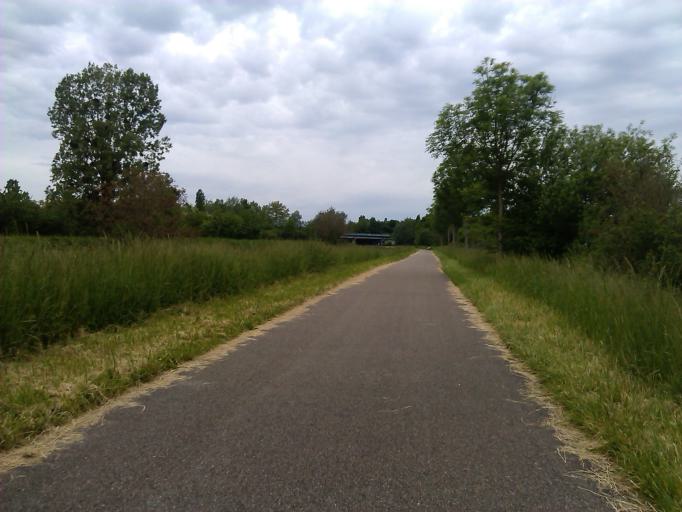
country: FR
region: Franche-Comte
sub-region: Departement du Jura
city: Choisey
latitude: 47.0574
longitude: 5.4411
